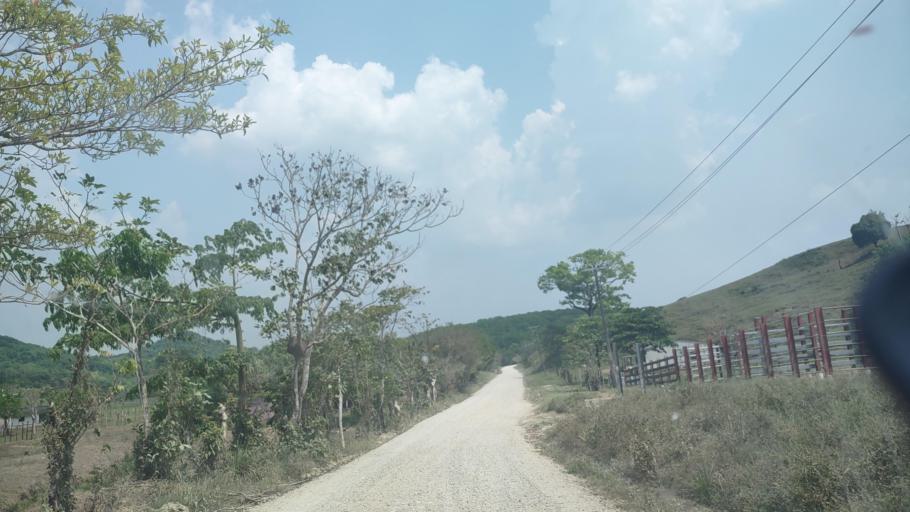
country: MX
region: Tabasco
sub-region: Huimanguillo
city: Francisco Rueda
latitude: 17.6080
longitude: -93.9084
